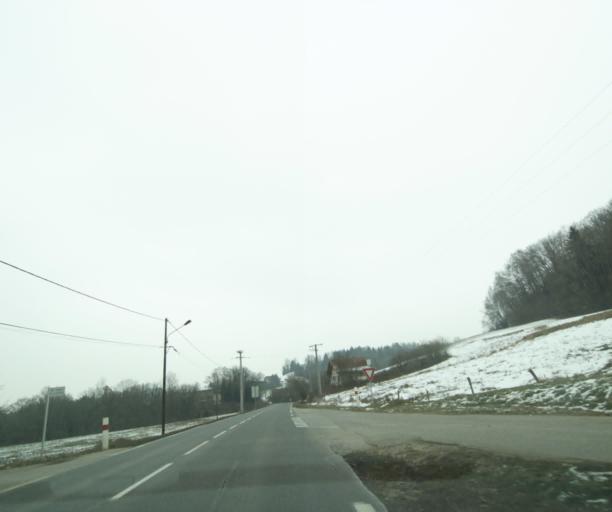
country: FR
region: Rhone-Alpes
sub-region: Departement de la Haute-Savoie
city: Arthaz-Pont-Notre-Dame
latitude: 46.1504
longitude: 6.2556
